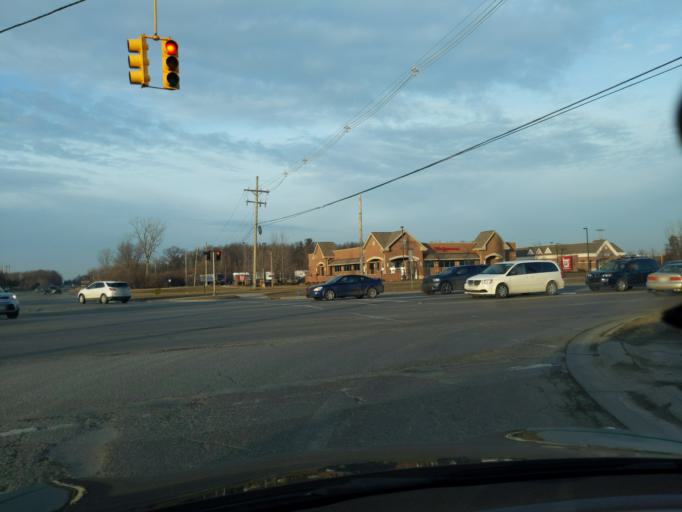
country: US
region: Michigan
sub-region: Livingston County
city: Brighton
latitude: 42.6329
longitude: -83.7530
